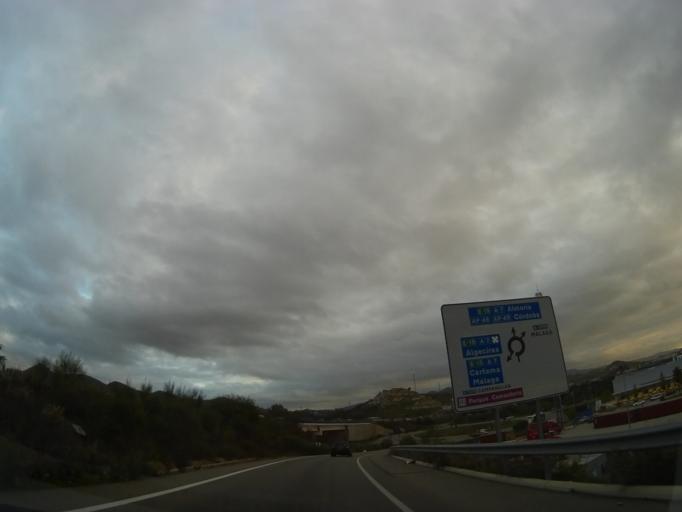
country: ES
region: Andalusia
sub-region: Provincia de Malaga
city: Alhaurin de la Torre
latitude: 36.7181
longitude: -4.5140
